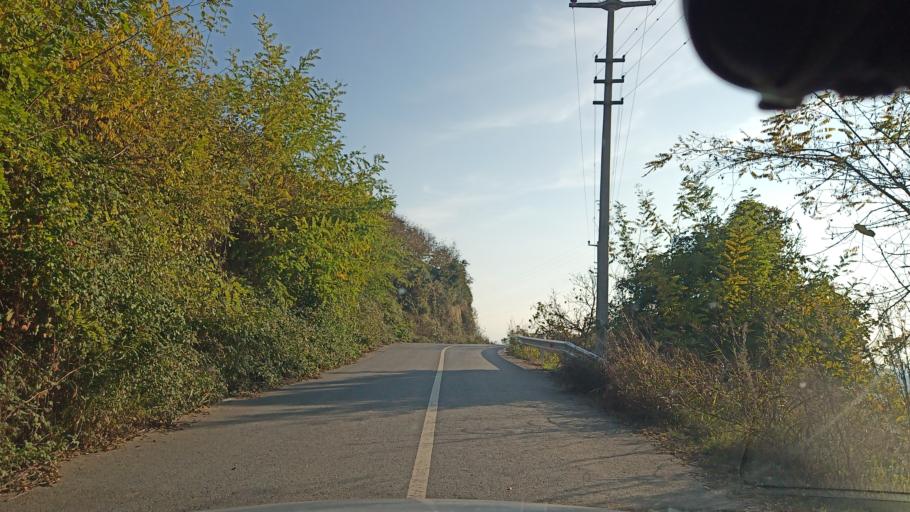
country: TR
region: Sakarya
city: Karasu
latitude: 41.0751
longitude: 30.6123
